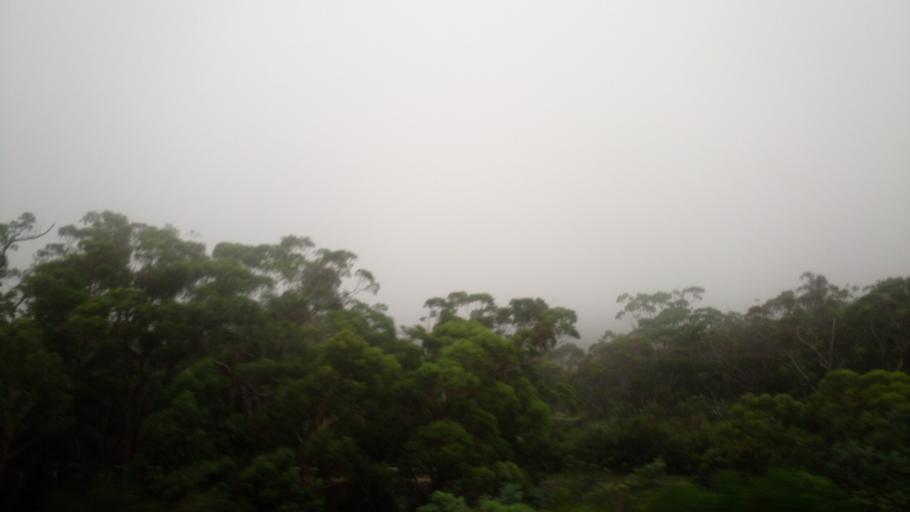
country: AU
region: New South Wales
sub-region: Blue Mountains Municipality
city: Lawson
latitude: -33.7168
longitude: 150.3843
